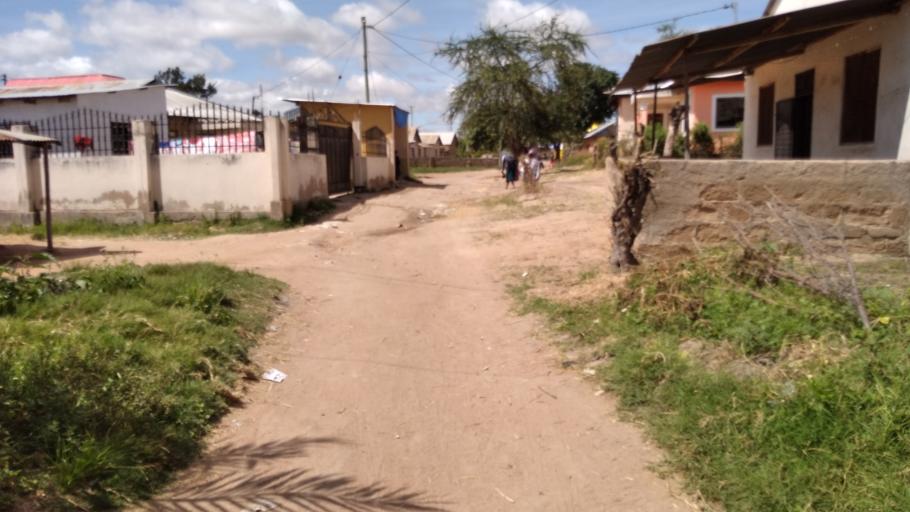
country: TZ
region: Dodoma
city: Dodoma
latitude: -6.1576
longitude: 35.7434
